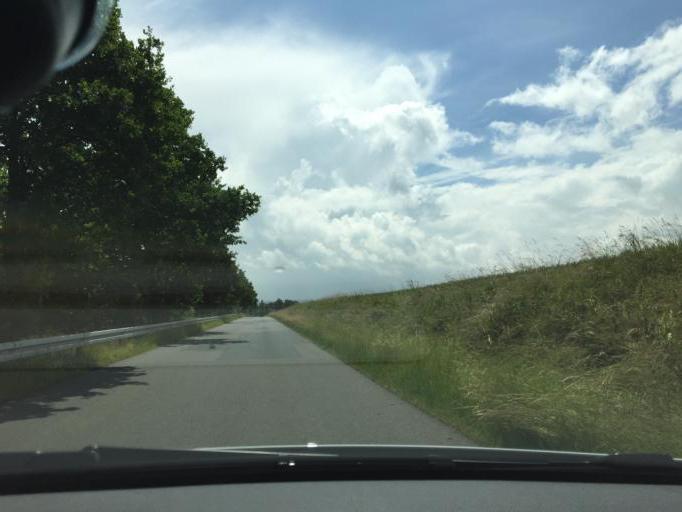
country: DE
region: Lower Saxony
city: Hehlen
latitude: 52.0272
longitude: 9.4127
